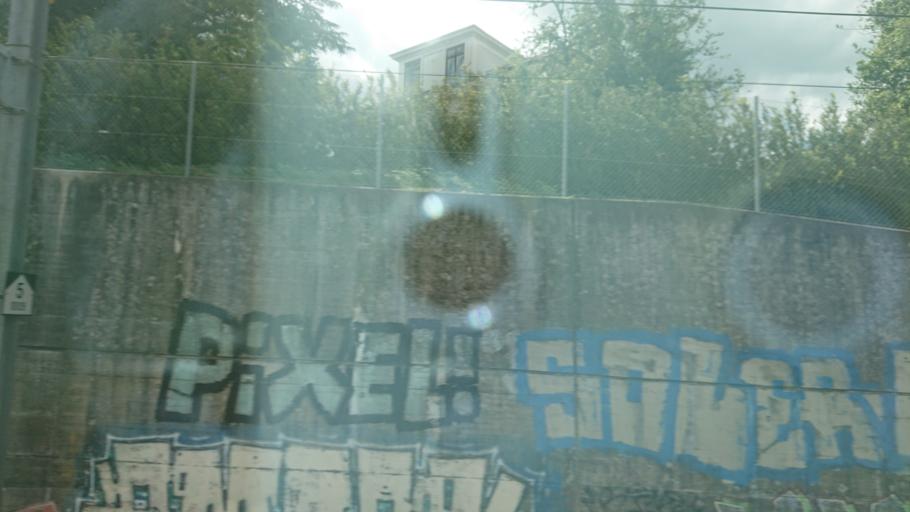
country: CH
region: Geneva
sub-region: Geneva
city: Versoix
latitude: 46.2747
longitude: 6.1662
